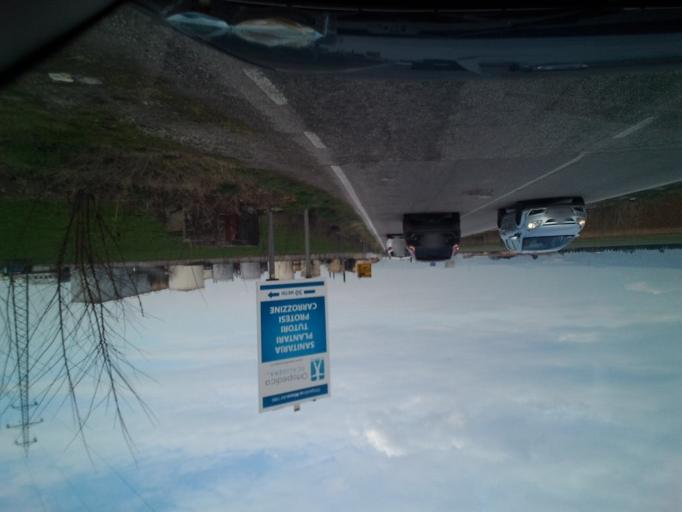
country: IT
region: Veneto
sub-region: Provincia di Verona
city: Sona
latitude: 45.4391
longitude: 10.8518
